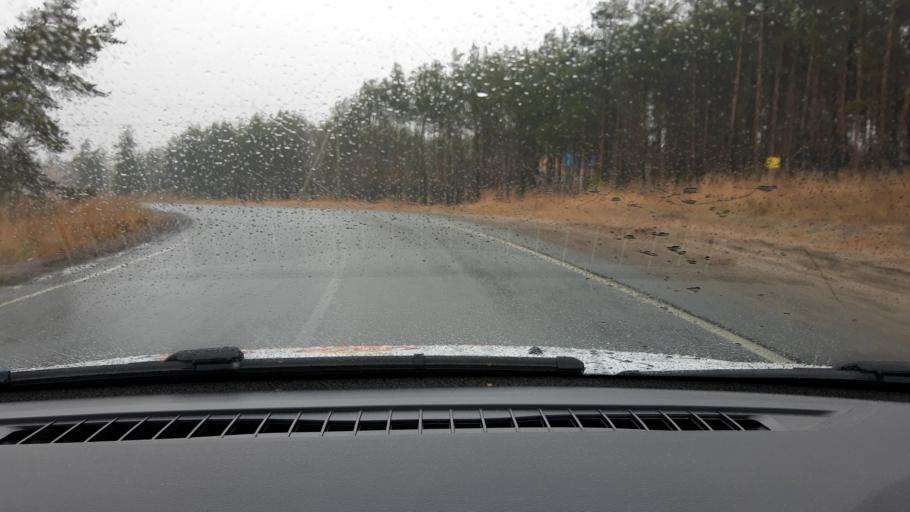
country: RU
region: Nizjnij Novgorod
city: Babino
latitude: 56.2981
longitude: 43.5971
